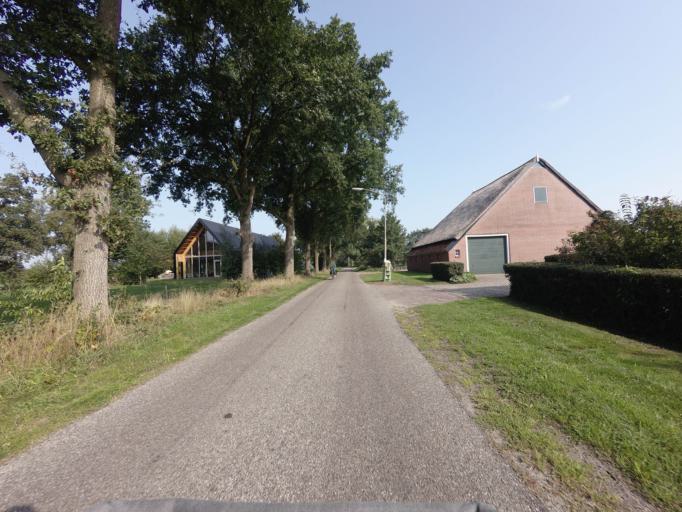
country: NL
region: Drenthe
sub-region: Gemeente Tynaarlo
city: Vries
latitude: 53.1286
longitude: 6.5269
